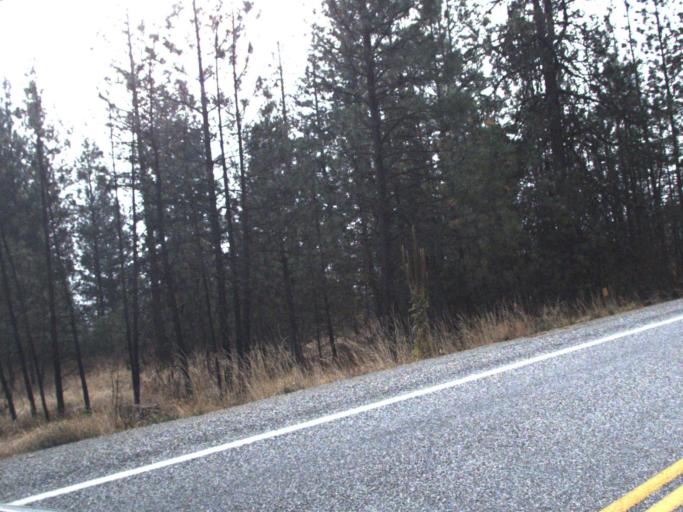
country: US
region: Washington
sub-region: Stevens County
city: Kettle Falls
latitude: 48.7663
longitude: -118.1405
